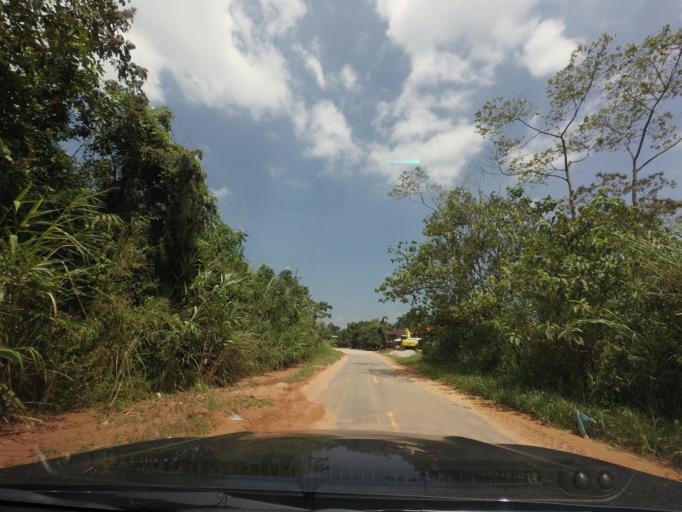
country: TH
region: Loei
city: Na Haeo
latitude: 17.5165
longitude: 100.8836
